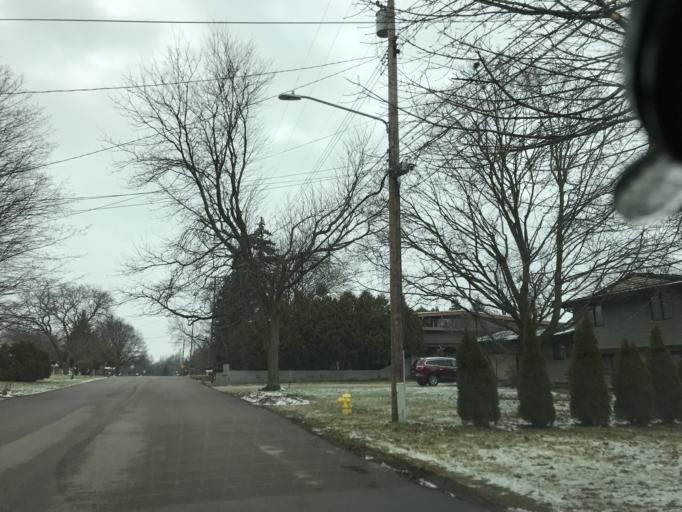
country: US
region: Michigan
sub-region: Kent County
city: East Grand Rapids
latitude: 42.9233
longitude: -85.5934
